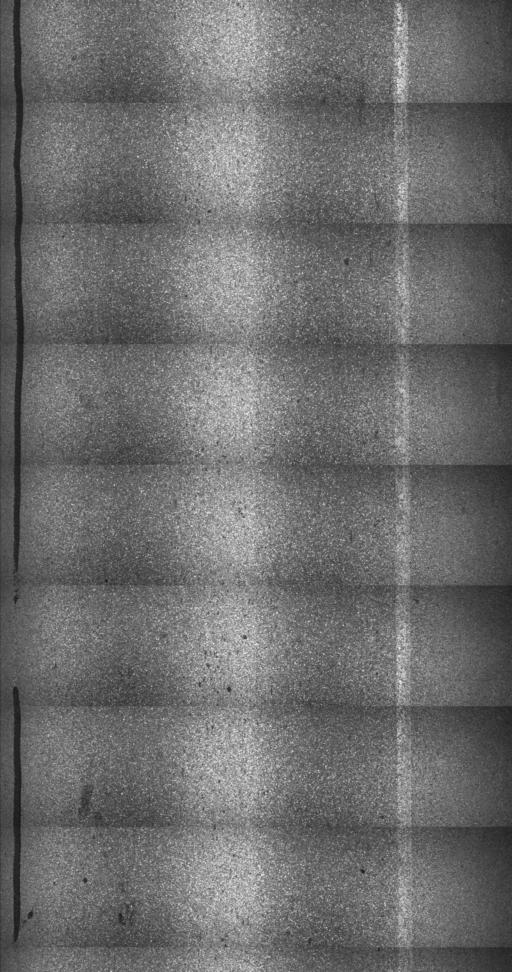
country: US
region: Vermont
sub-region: Franklin County
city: Enosburg Falls
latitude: 44.9028
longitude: -72.9435
